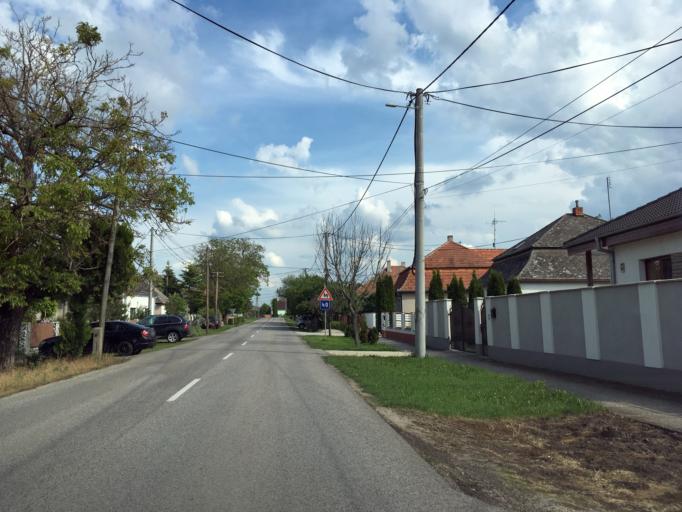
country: SK
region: Nitriansky
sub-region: Okres Komarno
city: Hurbanovo
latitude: 47.8125
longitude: 18.2202
